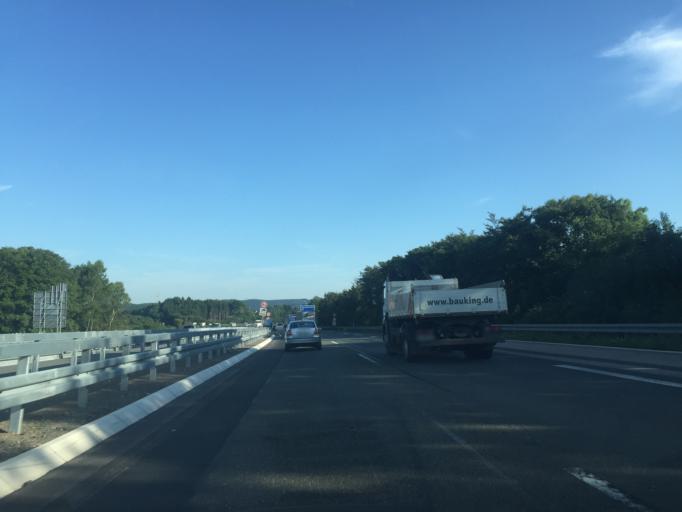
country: DE
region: North Rhine-Westphalia
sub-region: Regierungsbezirk Arnsberg
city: Luedenscheid
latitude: 51.2258
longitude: 7.6673
